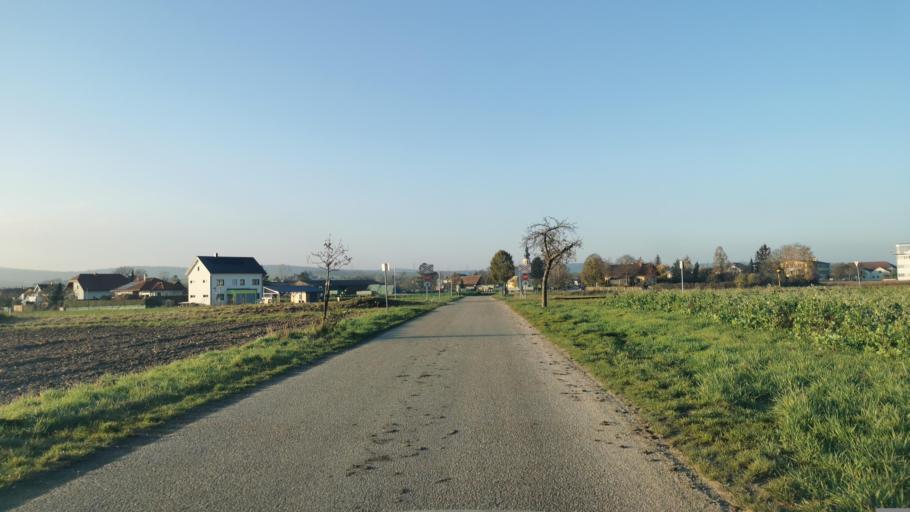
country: AT
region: Lower Austria
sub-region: Politischer Bezirk Korneuburg
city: Harmannsdorf
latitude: 48.3867
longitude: 16.3764
